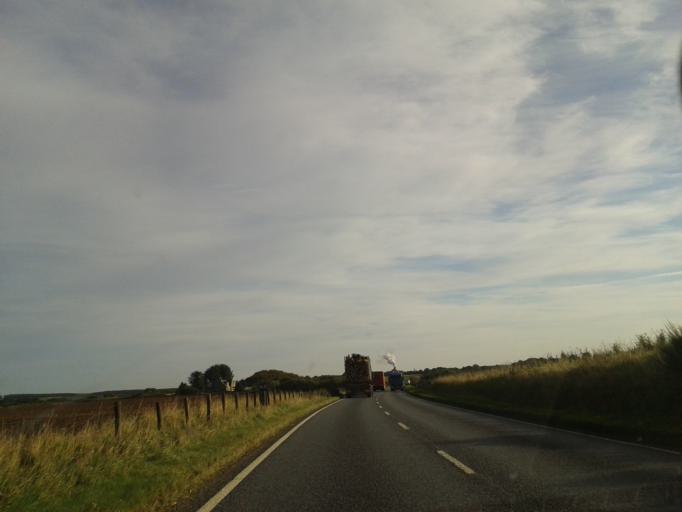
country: GB
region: Scotland
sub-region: Highland
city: Fortrose
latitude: 57.5078
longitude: -4.1121
